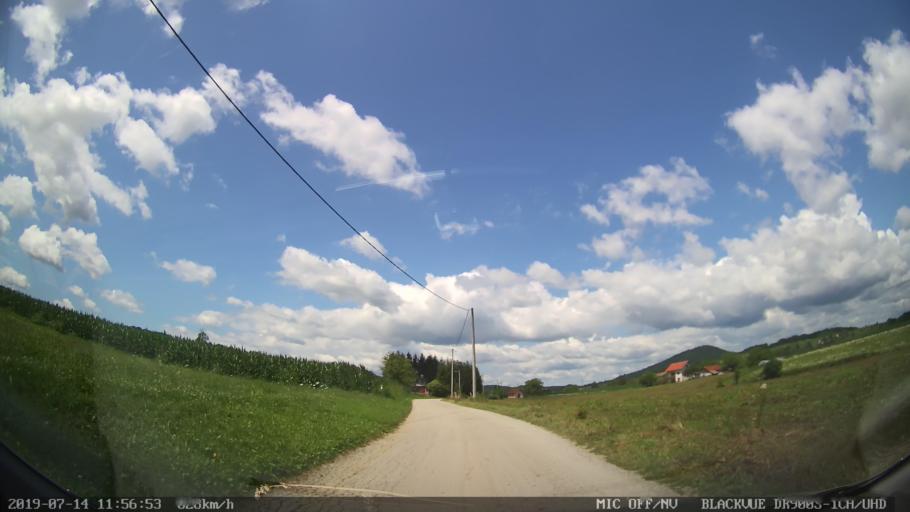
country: HR
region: Karlovacka
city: Vojnic
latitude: 45.3880
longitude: 15.6045
